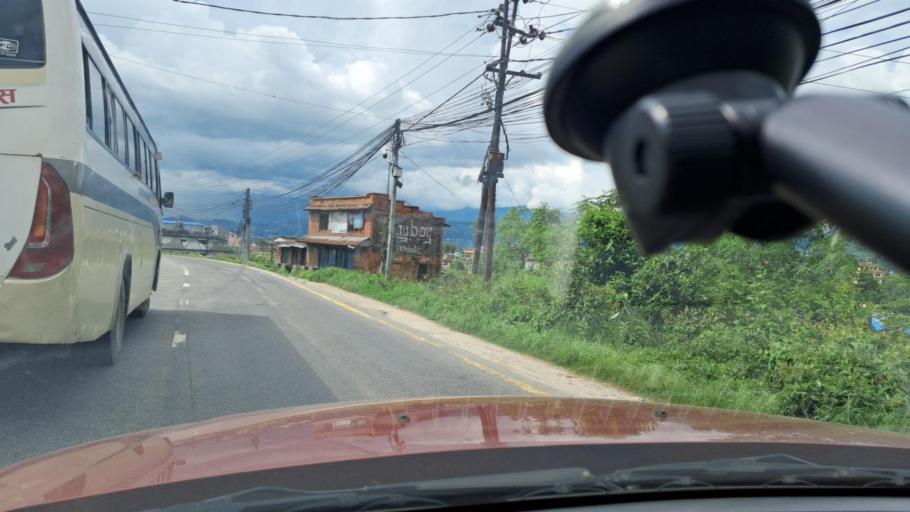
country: NP
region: Central Region
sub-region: Bagmati Zone
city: Hari Bdr Tamang House
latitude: 27.6511
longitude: 85.4623
